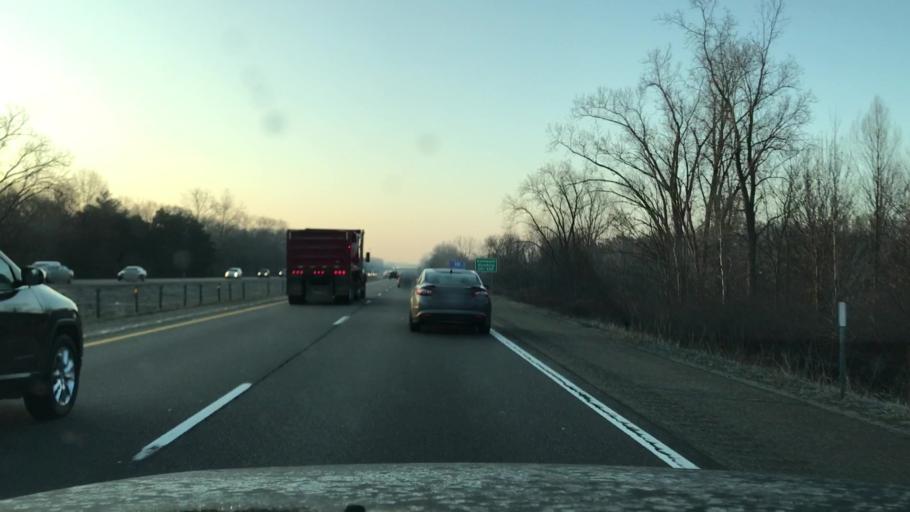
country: US
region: Michigan
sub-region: Kent County
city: East Grand Rapids
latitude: 42.9259
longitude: -85.5556
